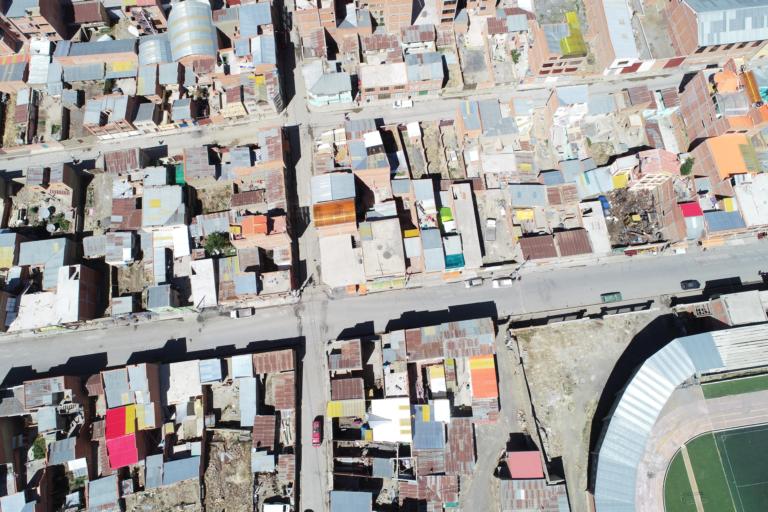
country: BO
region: La Paz
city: Achacachi
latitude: -16.0459
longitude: -68.6827
